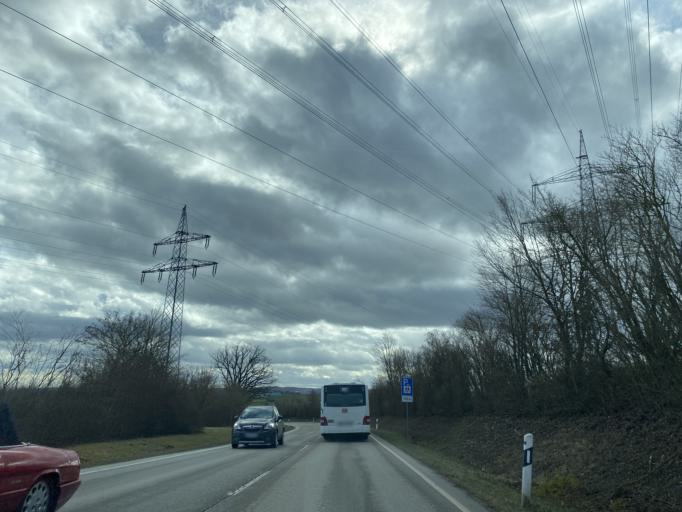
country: DE
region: Baden-Wuerttemberg
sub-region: Regierungsbezirk Stuttgart
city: Hemmingen
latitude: 48.8474
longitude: 8.9968
